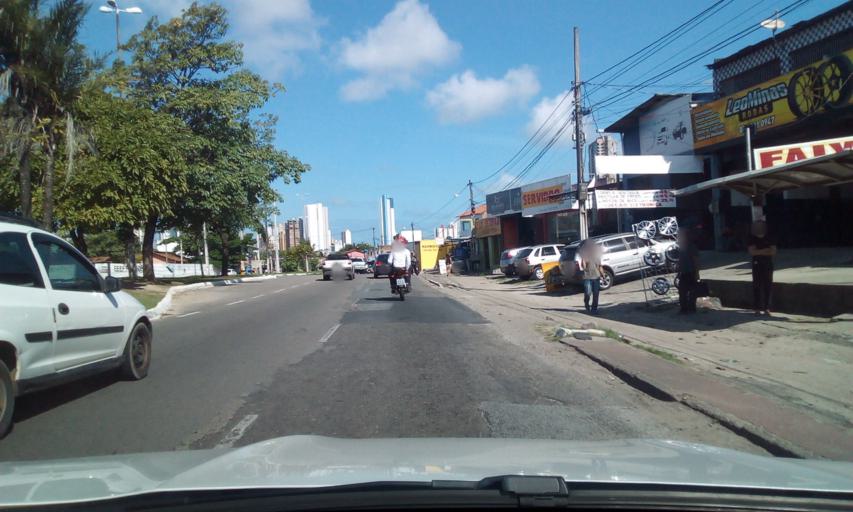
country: BR
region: Paraiba
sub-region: Joao Pessoa
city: Joao Pessoa
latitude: -7.0983
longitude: -34.8537
